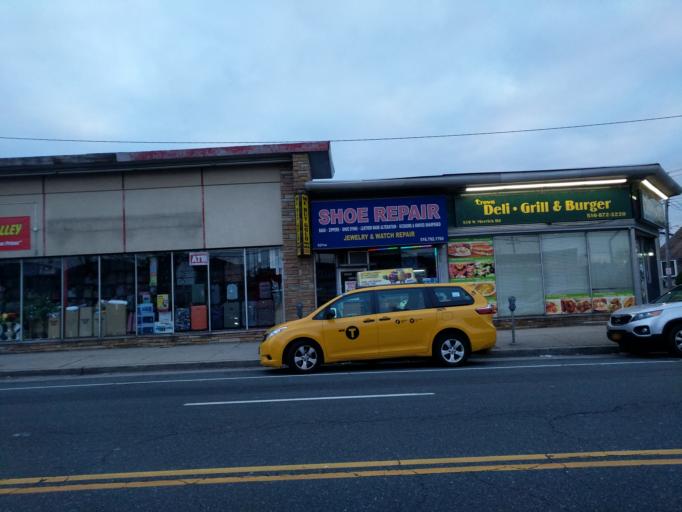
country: US
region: New York
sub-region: Nassau County
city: Valley Stream
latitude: 40.6699
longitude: -73.7162
